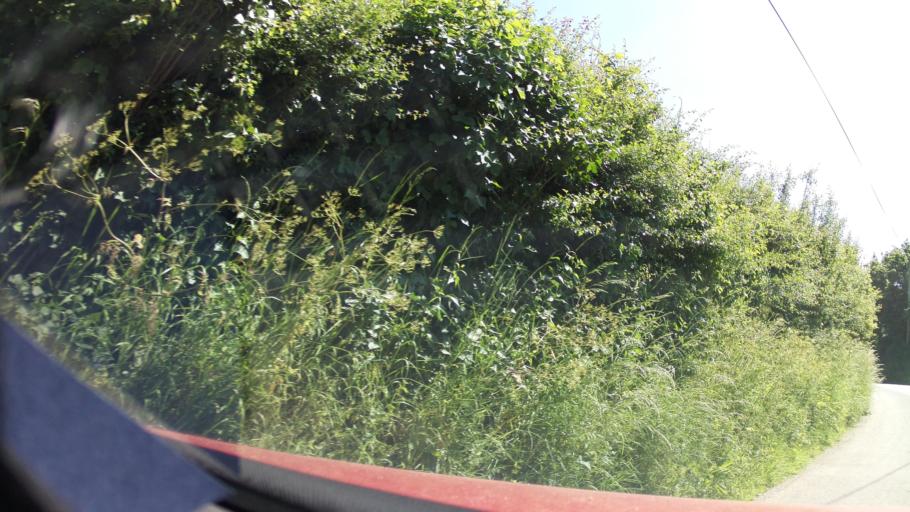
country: GB
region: England
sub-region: Wiltshire
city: Bremhill
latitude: 51.4474
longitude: -2.0285
